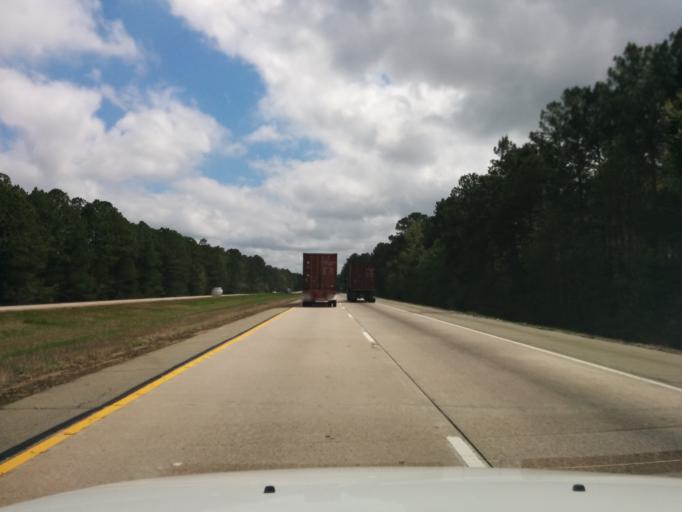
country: US
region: Georgia
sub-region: Bryan County
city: Pembroke
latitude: 32.1991
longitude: -81.4839
